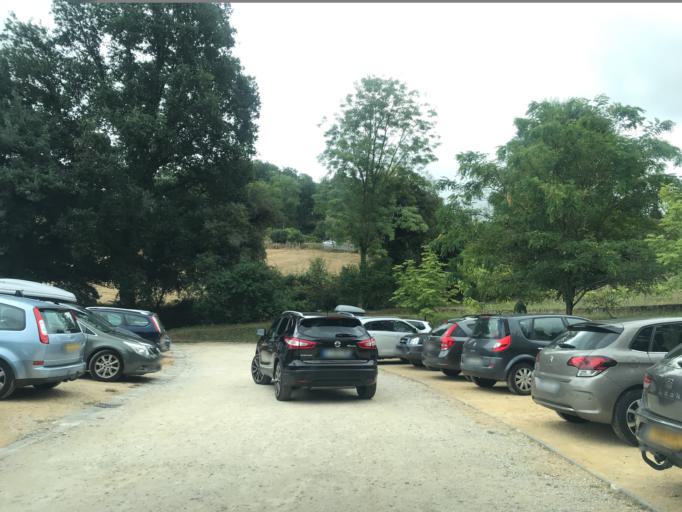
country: FR
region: Aquitaine
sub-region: Departement de la Dordogne
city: Domme
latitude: 44.8030
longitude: 1.2186
